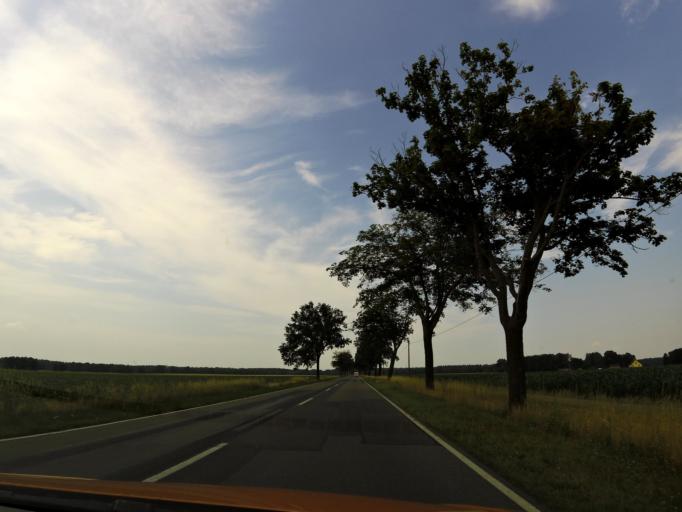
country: DE
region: Brandenburg
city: Wusterhausen
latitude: 52.9005
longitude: 12.4494
